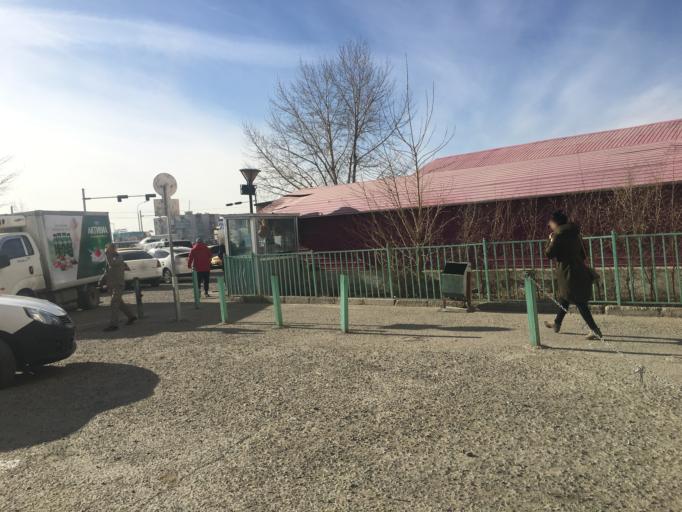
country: MN
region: Ulaanbaatar
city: Ulaanbaatar
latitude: 47.9104
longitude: 106.8028
